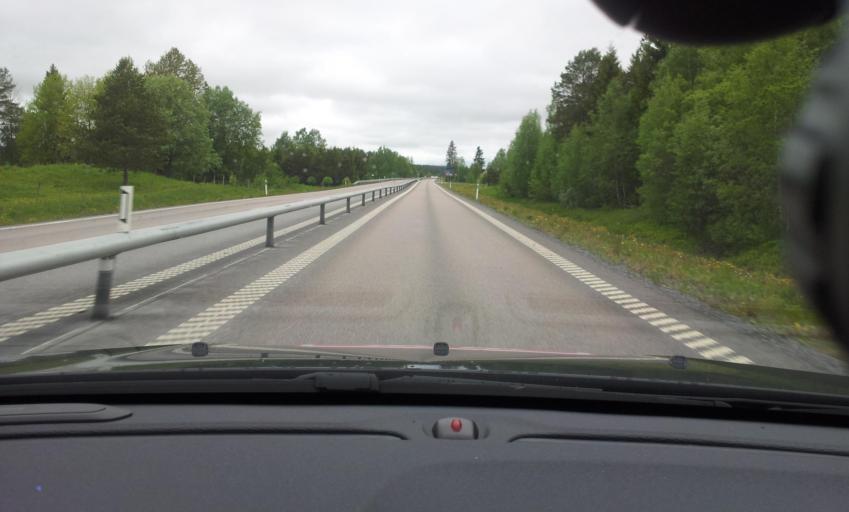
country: SE
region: Jaemtland
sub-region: Krokoms Kommun
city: Krokom
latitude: 63.3118
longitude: 14.4730
